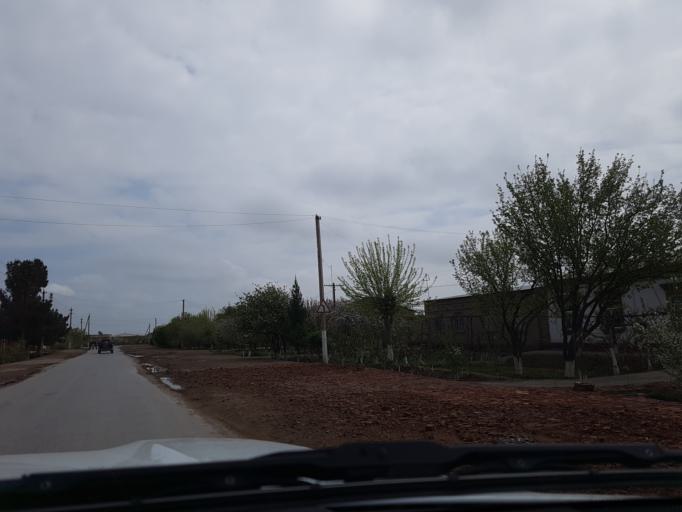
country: TM
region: Lebap
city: Turkmenabat
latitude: 38.9715
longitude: 63.6841
